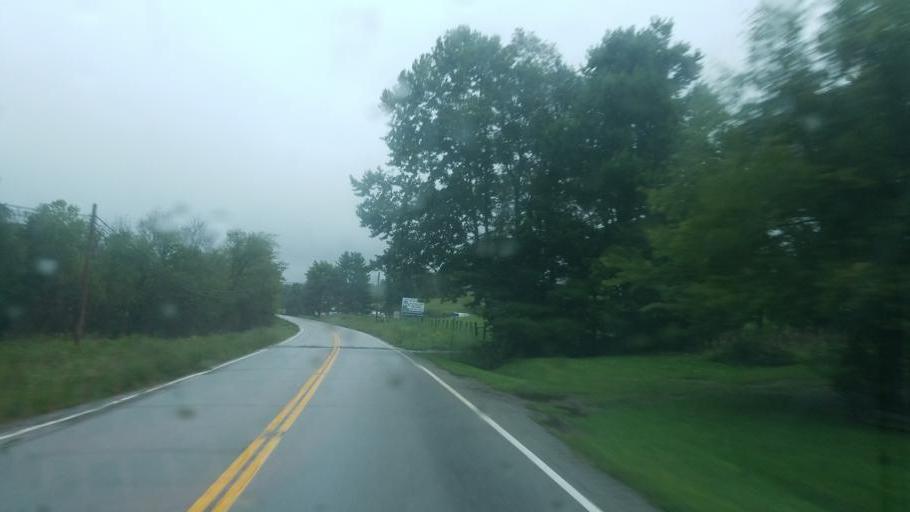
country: US
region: Kentucky
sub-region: Fleming County
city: Flemingsburg
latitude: 38.3720
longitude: -83.6302
